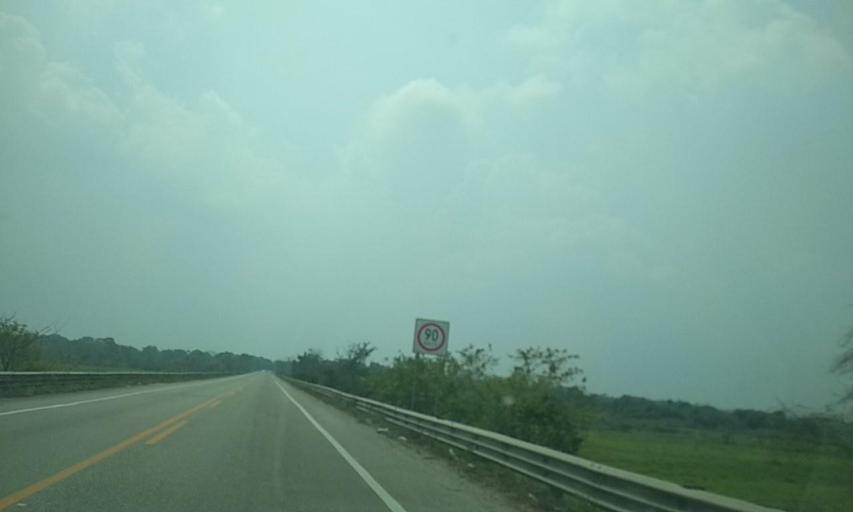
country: MX
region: Tabasco
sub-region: Huimanguillo
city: Francisco Rueda
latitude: 17.7691
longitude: -94.0359
